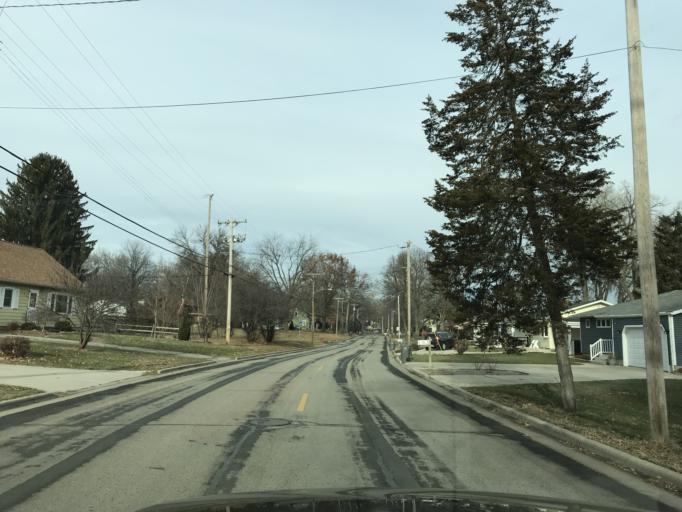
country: US
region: Wisconsin
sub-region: Dane County
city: Monona
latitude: 43.0622
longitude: -89.3457
